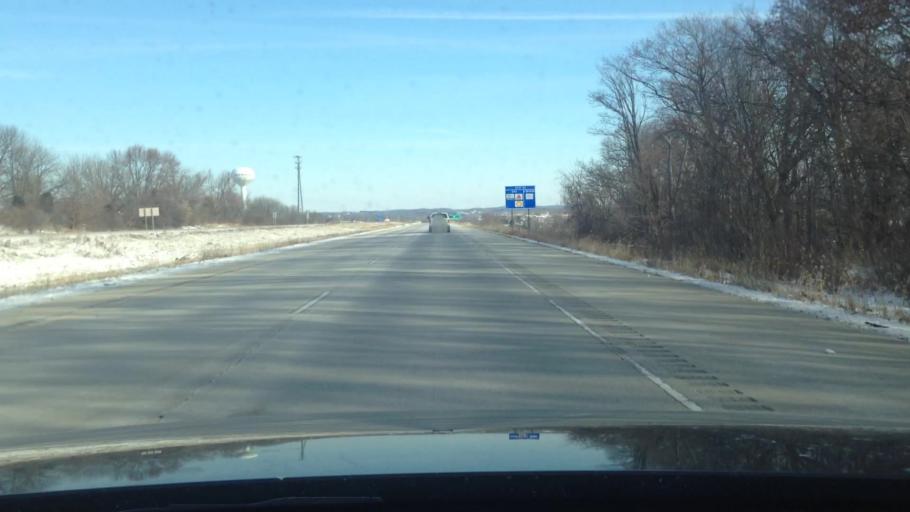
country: US
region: Wisconsin
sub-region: Waukesha County
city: Mukwonago
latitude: 42.8438
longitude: -88.3319
